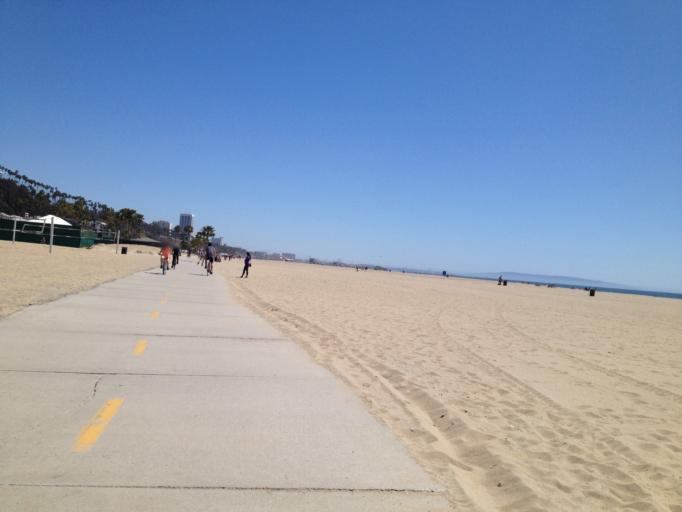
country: US
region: California
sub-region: Los Angeles County
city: Santa Monica
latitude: 34.0267
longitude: -118.5187
